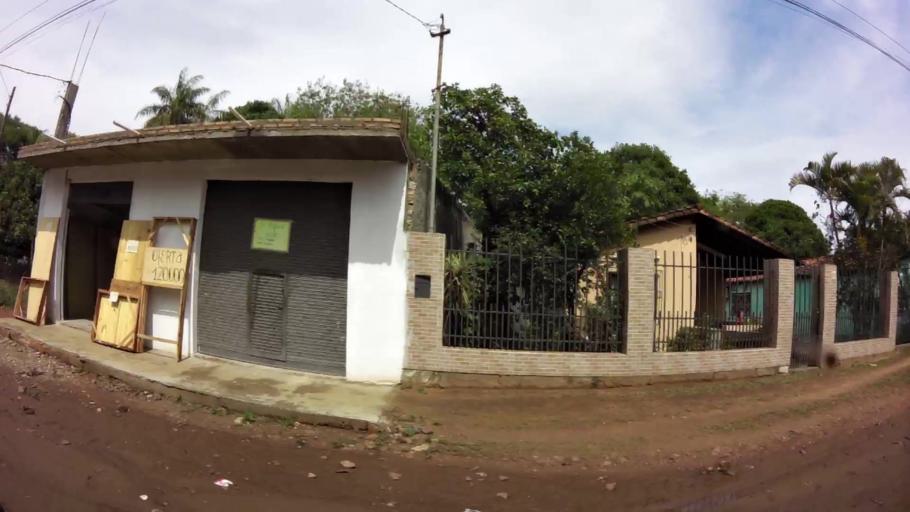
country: PY
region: Central
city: Limpio
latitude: -25.1820
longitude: -57.4663
